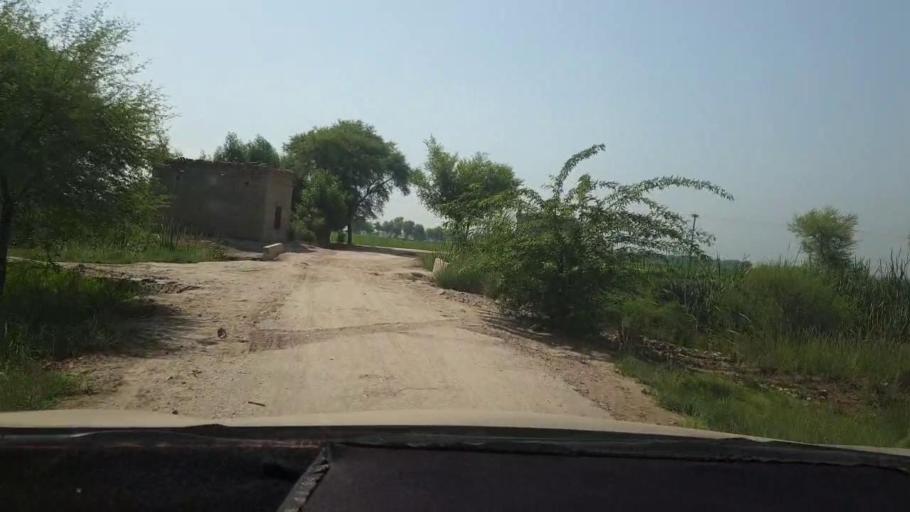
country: PK
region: Sindh
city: Miro Khan
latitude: 27.7086
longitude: 68.0391
